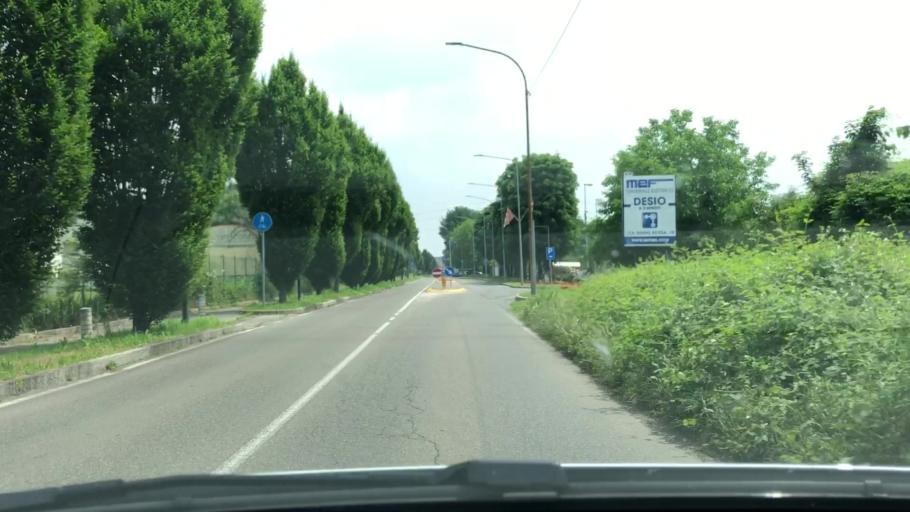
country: IT
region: Lombardy
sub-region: Provincia di Monza e Brianza
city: Desio
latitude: 45.6255
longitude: 9.1856
